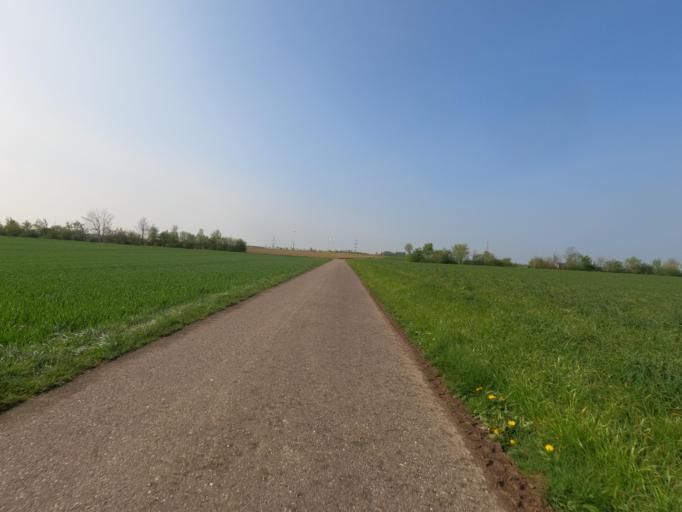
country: DE
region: North Rhine-Westphalia
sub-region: Regierungsbezirk Koln
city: Heinsberg
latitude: 51.0387
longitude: 6.1246
